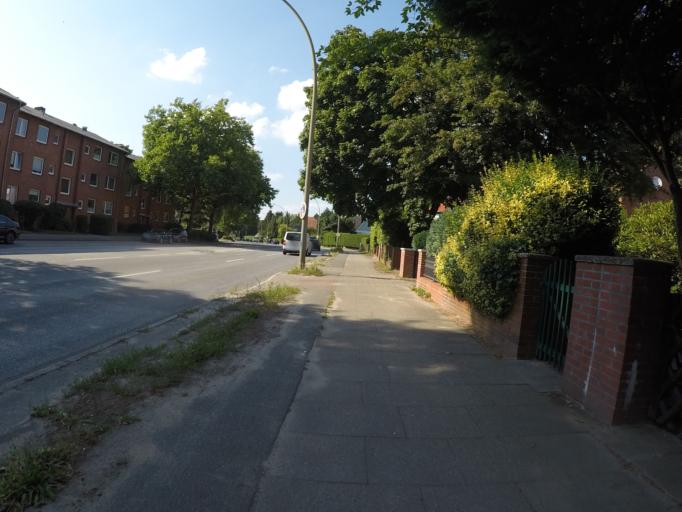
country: DE
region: Hamburg
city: Farmsen-Berne
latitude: 53.6256
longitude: 10.1455
